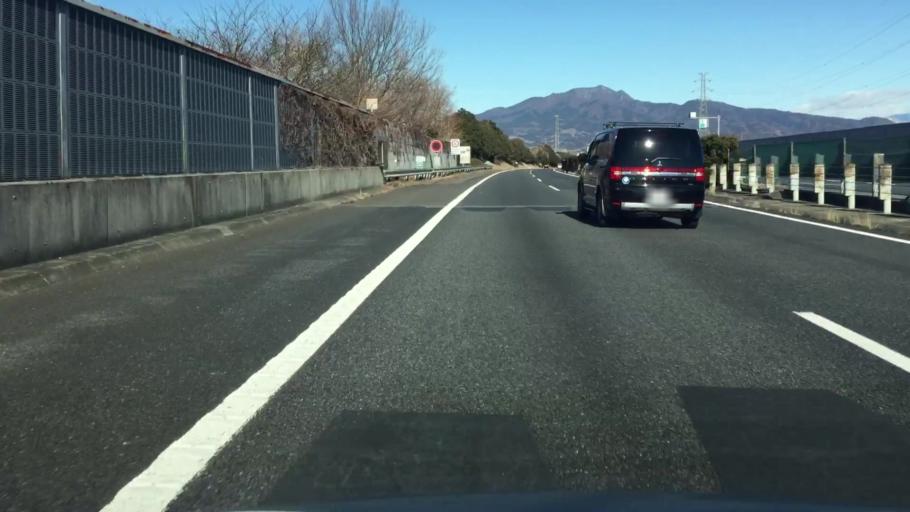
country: JP
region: Gunma
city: Shibukawa
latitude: 36.4606
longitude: 139.0120
